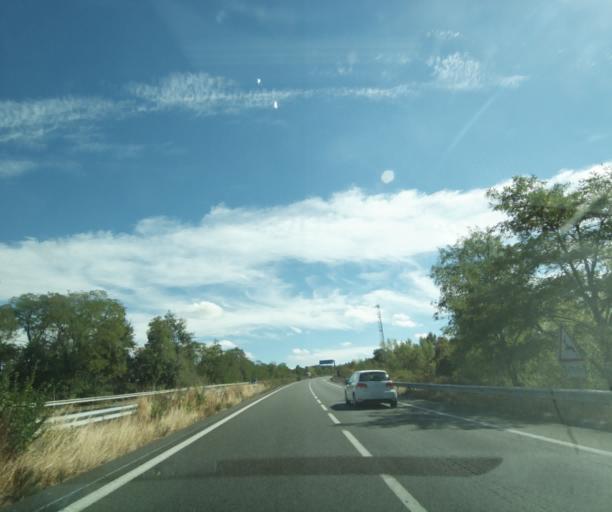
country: FR
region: Midi-Pyrenees
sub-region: Departement du Tarn-et-Garonne
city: Lamagistere
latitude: 44.0888
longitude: 0.7925
